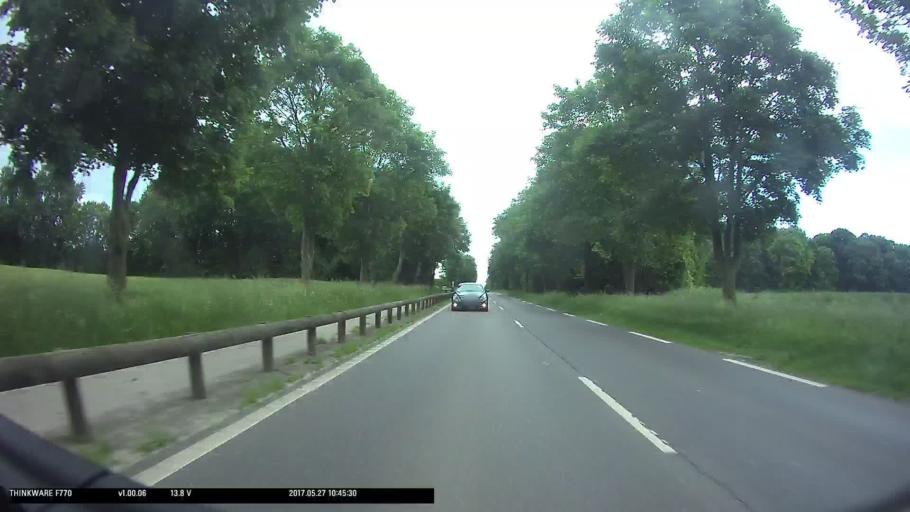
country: FR
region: Ile-de-France
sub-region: Departement du Val-d'Oise
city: Chars
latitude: 49.1552
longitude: 1.9533
